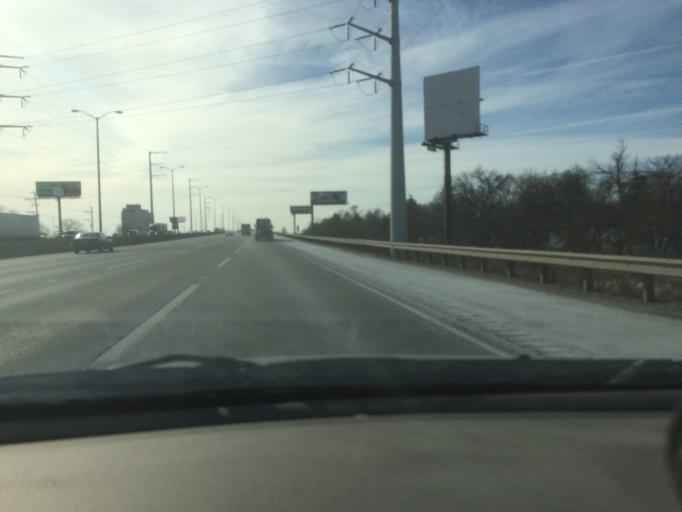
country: US
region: Illinois
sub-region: DuPage County
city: Elmhurst
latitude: 41.9130
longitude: -87.9200
